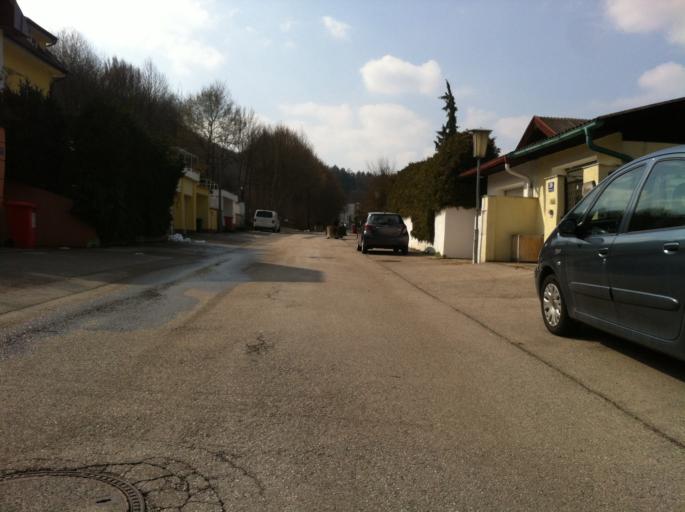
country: AT
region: Lower Austria
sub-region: Politischer Bezirk Wien-Umgebung
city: Purkersdorf
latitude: 48.1985
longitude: 16.1647
